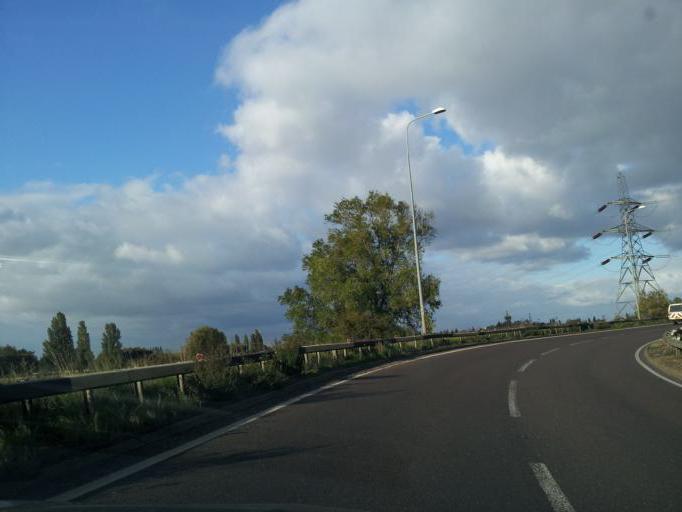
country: GB
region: England
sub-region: Cambridgeshire
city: Eaton Socon
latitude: 52.2037
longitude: -0.2981
